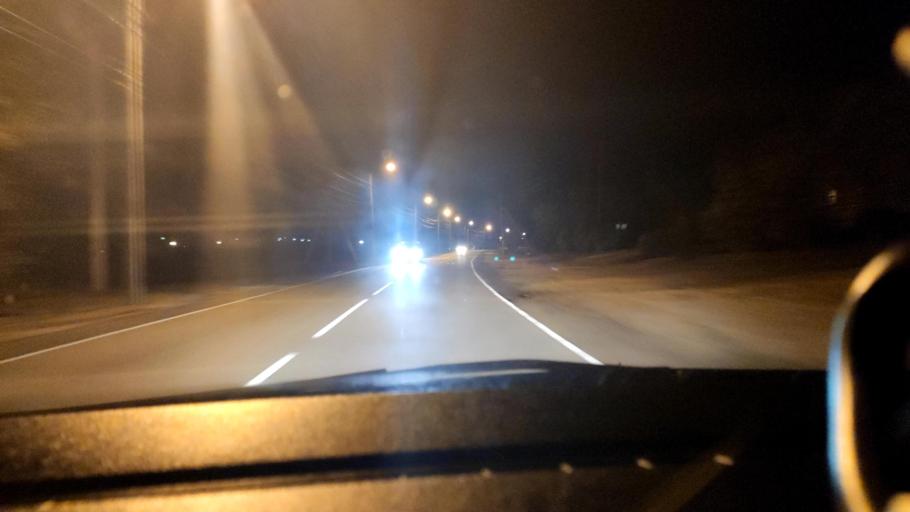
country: RU
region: Voronezj
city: Shilovo
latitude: 51.5498
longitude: 39.0816
